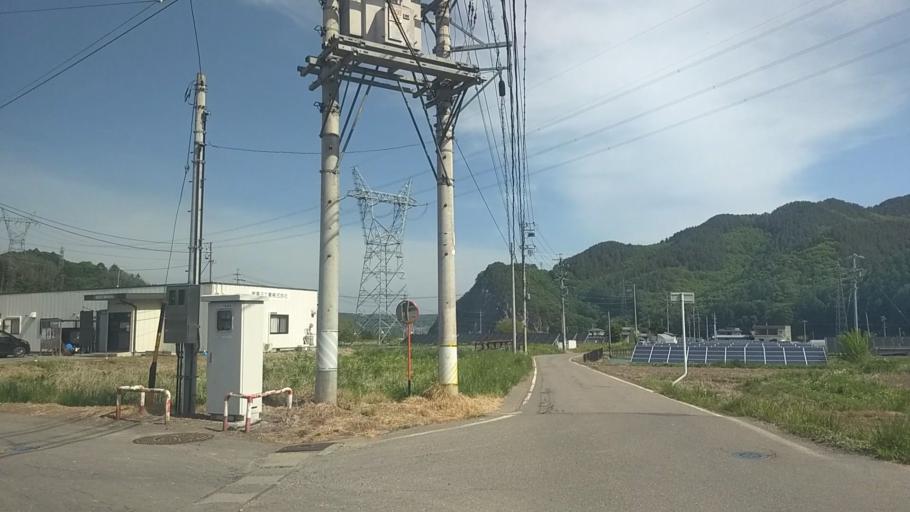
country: JP
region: Nagano
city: Saku
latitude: 36.1031
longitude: 138.4842
